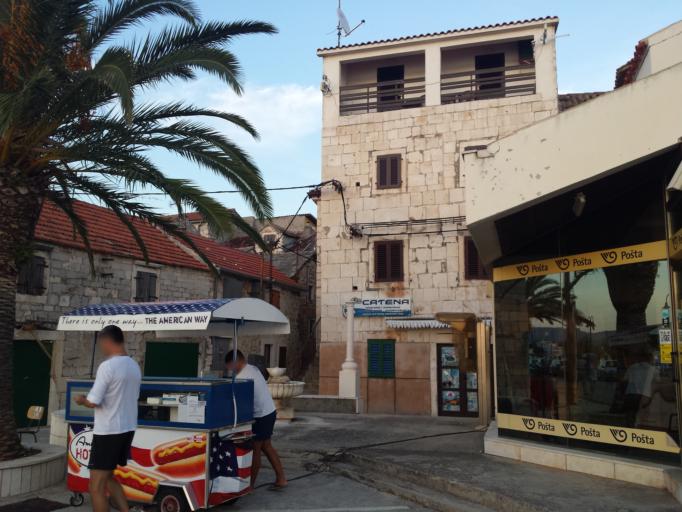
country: HR
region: Sibensko-Kniniska
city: Rogoznica
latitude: 43.5283
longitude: 15.9680
